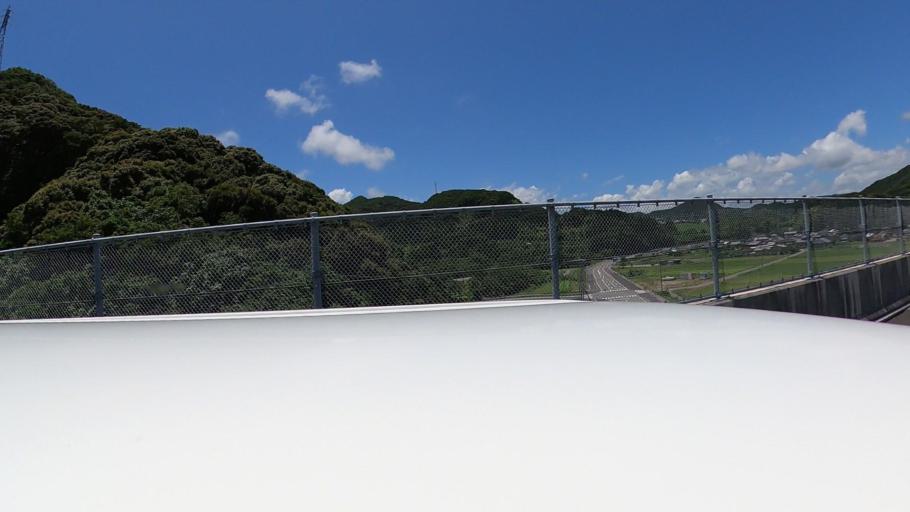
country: JP
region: Miyazaki
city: Nobeoka
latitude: 32.3965
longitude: 131.6195
